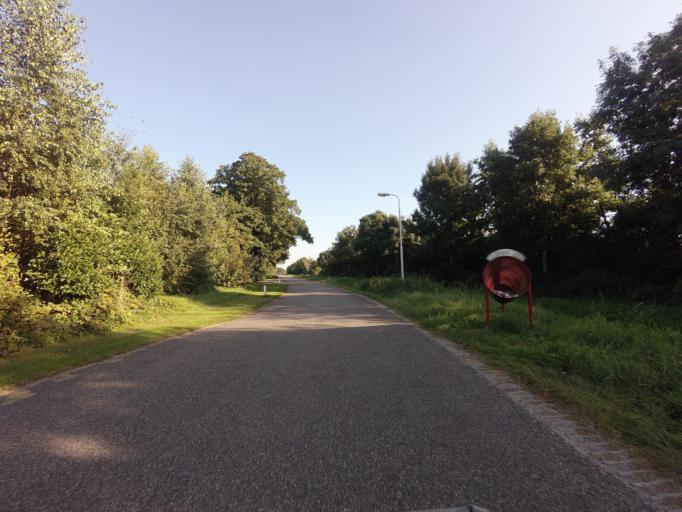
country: NL
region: Overijssel
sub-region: Gemeente Hardenberg
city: Hardenberg
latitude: 52.5593
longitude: 6.6412
